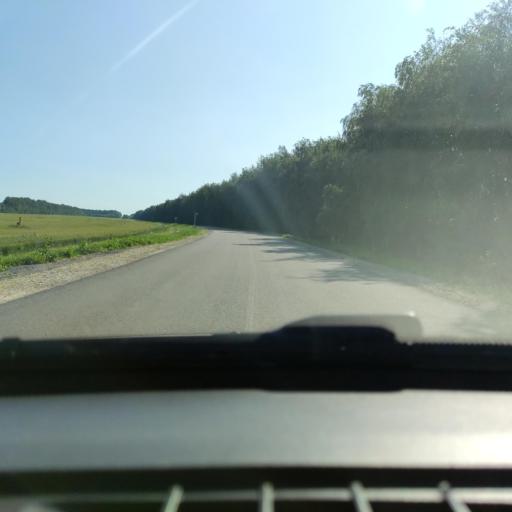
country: RU
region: Voronezj
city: Pereleshinskiy
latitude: 51.6444
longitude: 40.2918
